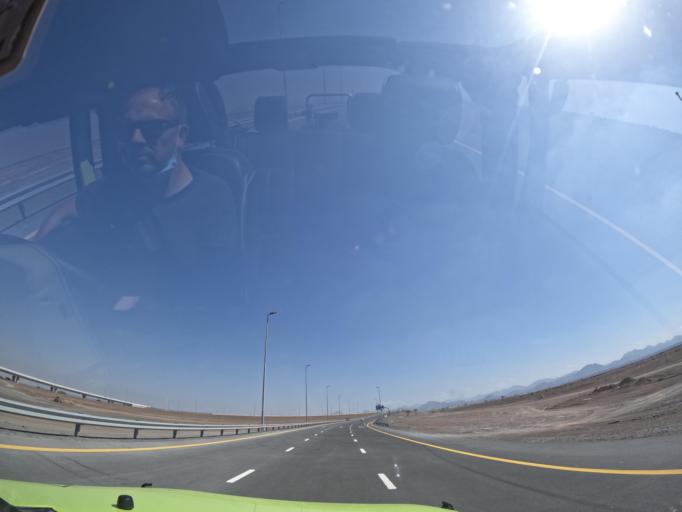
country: AE
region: Ash Shariqah
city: Adh Dhayd
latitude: 25.1165
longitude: 55.9418
